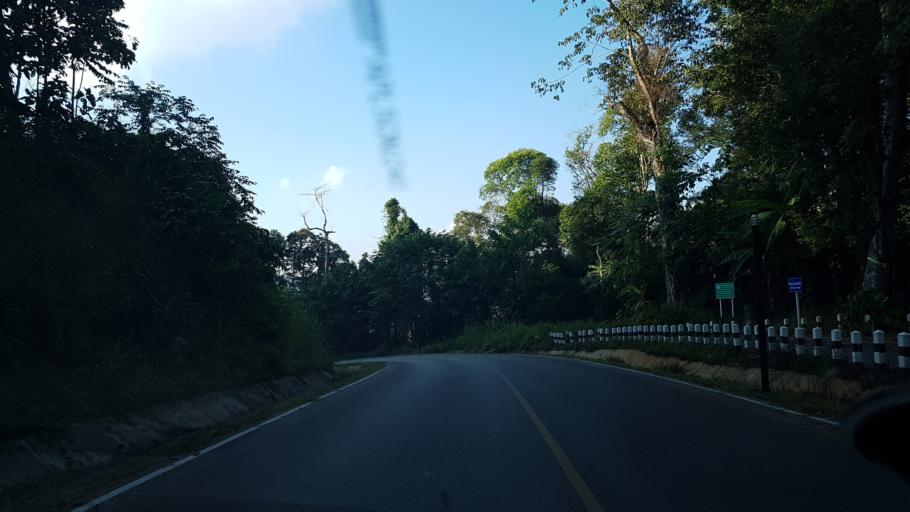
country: TH
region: Chiang Rai
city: Mae Fa Luang
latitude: 20.3258
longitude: 99.8329
